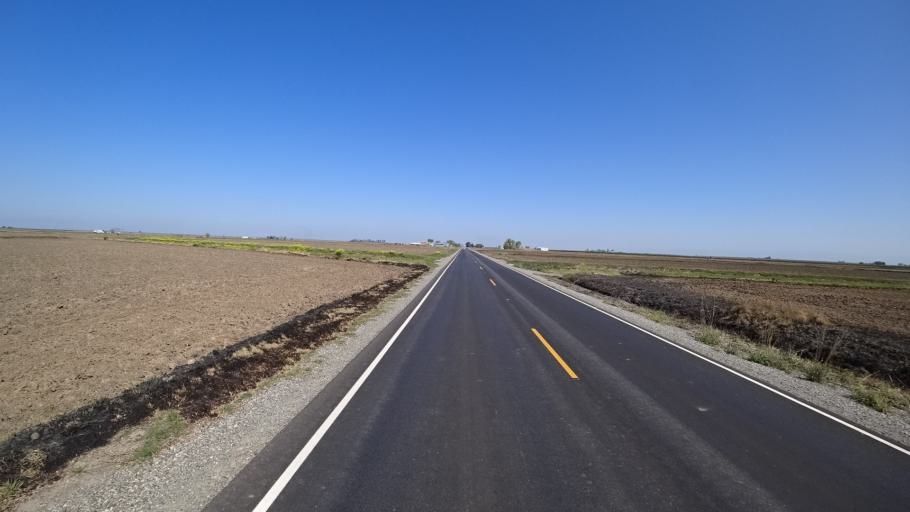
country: US
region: California
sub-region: Glenn County
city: Hamilton City
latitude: 39.6063
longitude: -122.0651
